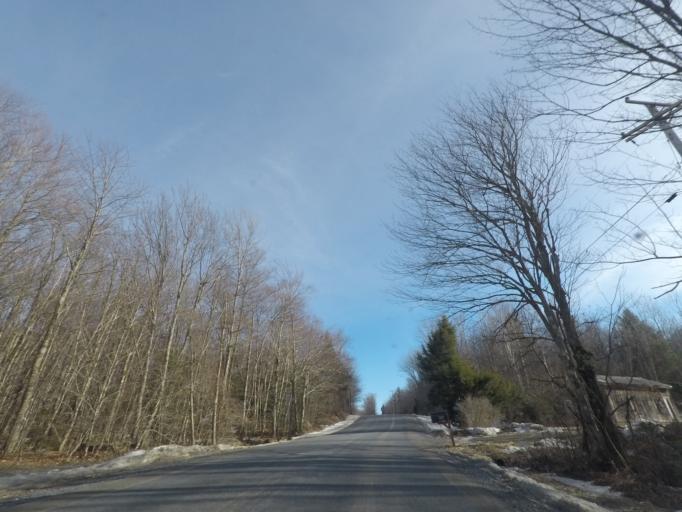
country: US
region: New York
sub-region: Rensselaer County
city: Poestenkill
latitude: 42.7530
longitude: -73.4188
